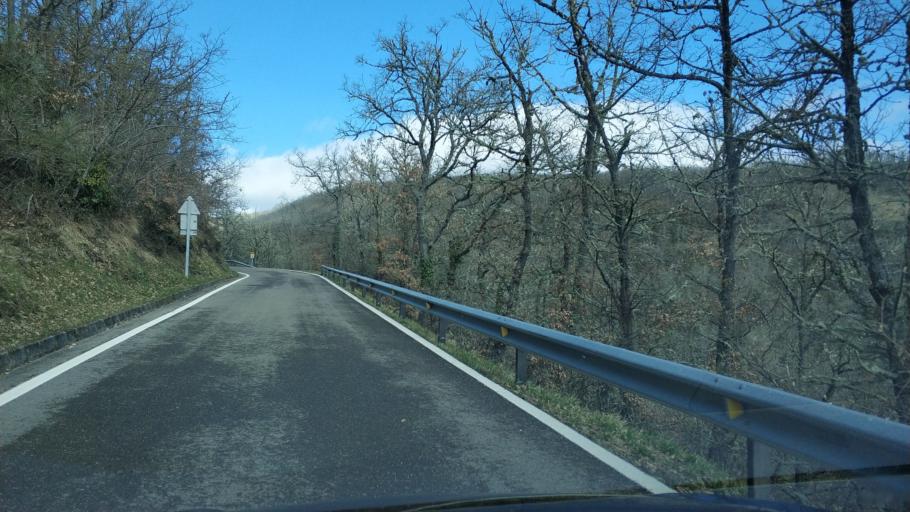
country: ES
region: Castille and Leon
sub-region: Provincia de Palencia
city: Berzosilla
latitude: 42.8983
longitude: -4.0417
